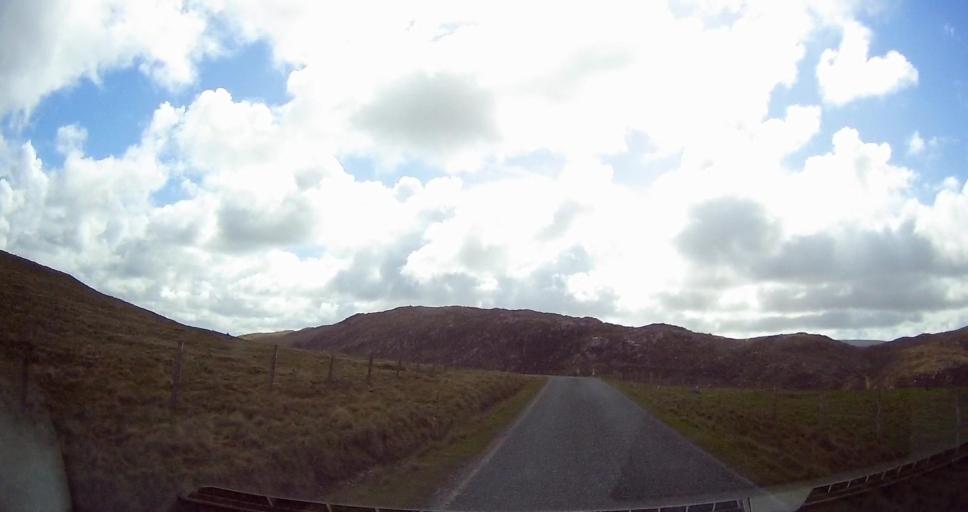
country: GB
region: Scotland
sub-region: Shetland Islands
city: Lerwick
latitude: 60.5578
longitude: -1.3371
